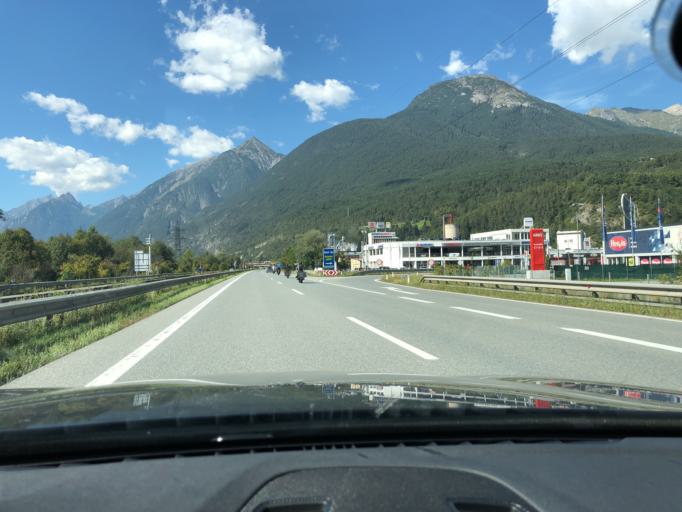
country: AT
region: Tyrol
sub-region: Politischer Bezirk Imst
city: Imst
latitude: 47.2168
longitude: 10.7374
